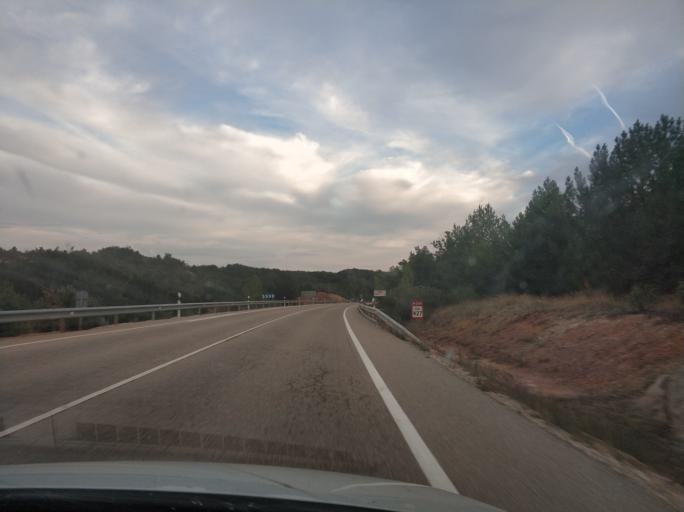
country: ES
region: Castille and Leon
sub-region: Provincia de Burgos
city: Pinilla de los Barruecos
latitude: 41.9258
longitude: -3.2791
